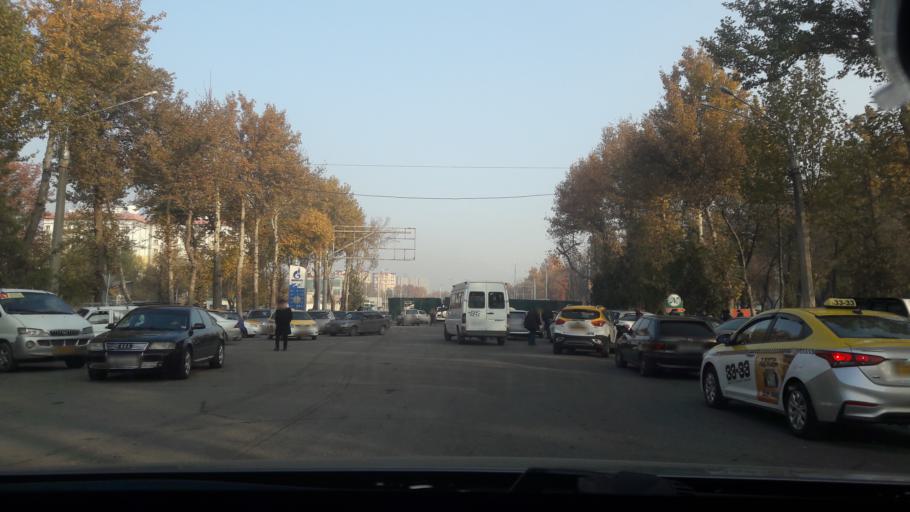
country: TJ
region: Dushanbe
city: Dushanbe
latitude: 38.5804
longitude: 68.7551
